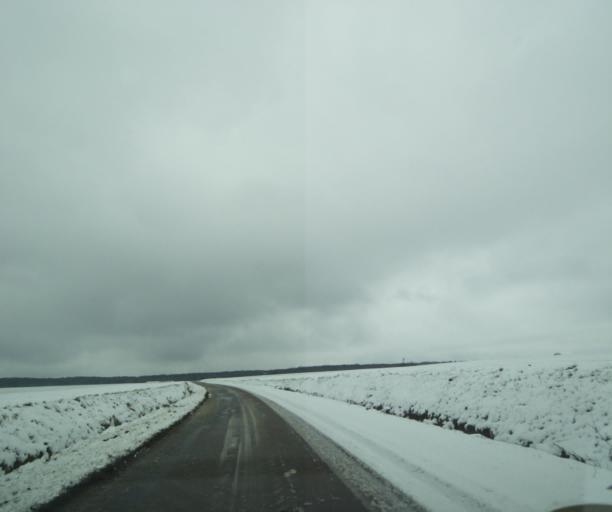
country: FR
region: Champagne-Ardenne
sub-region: Departement de la Haute-Marne
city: Laneuville-a-Remy
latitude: 48.4022
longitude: 4.8545
